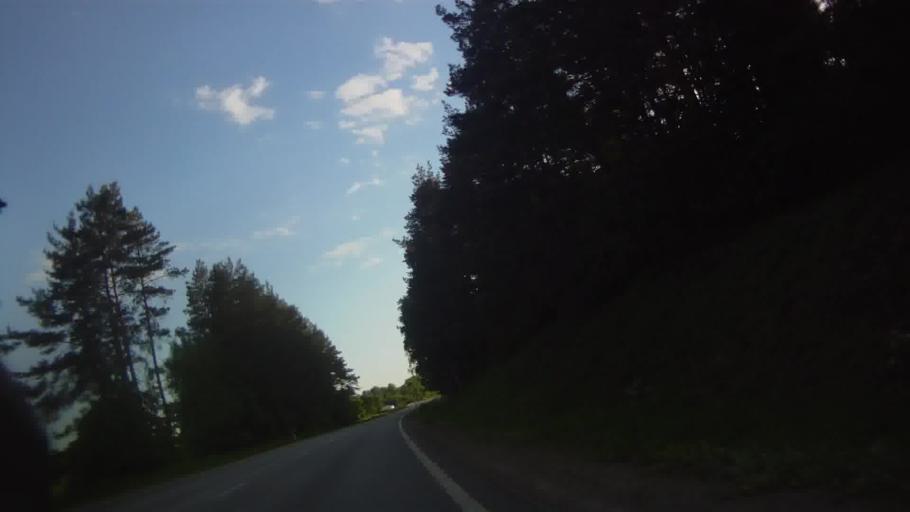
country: LV
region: Varaklani
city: Varaklani
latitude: 56.5700
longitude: 26.6488
